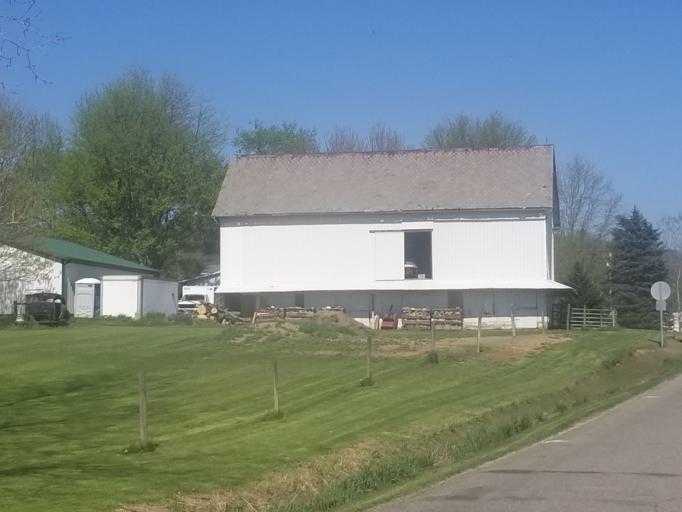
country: US
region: Ohio
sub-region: Medina County
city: Westfield Center
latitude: 40.9981
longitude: -81.9608
